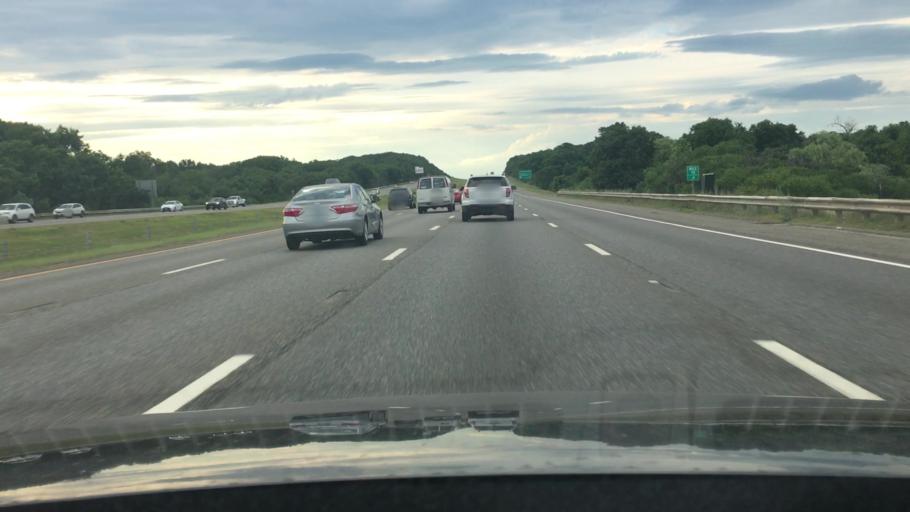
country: US
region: Massachusetts
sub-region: Essex County
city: Topsfield
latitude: 42.6007
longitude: -70.9664
